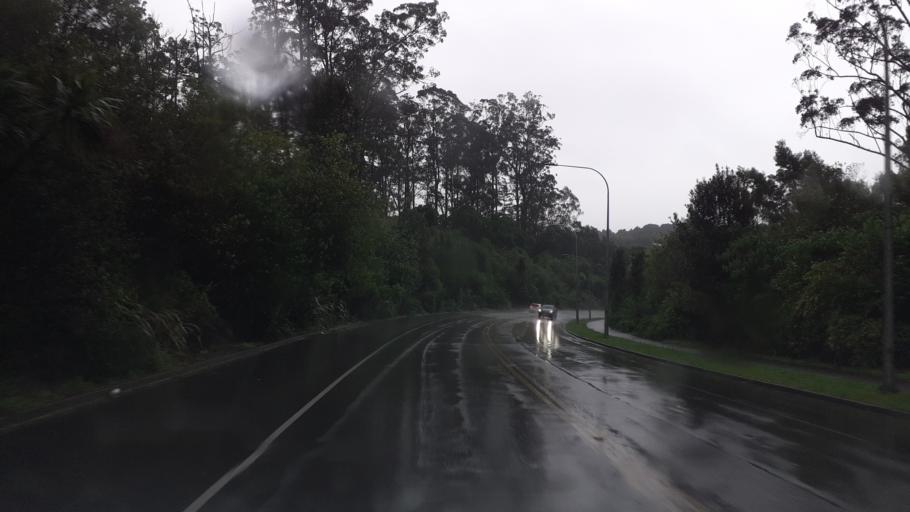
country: NZ
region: Northland
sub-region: Far North District
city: Kerikeri
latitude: -35.2204
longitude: 173.9520
